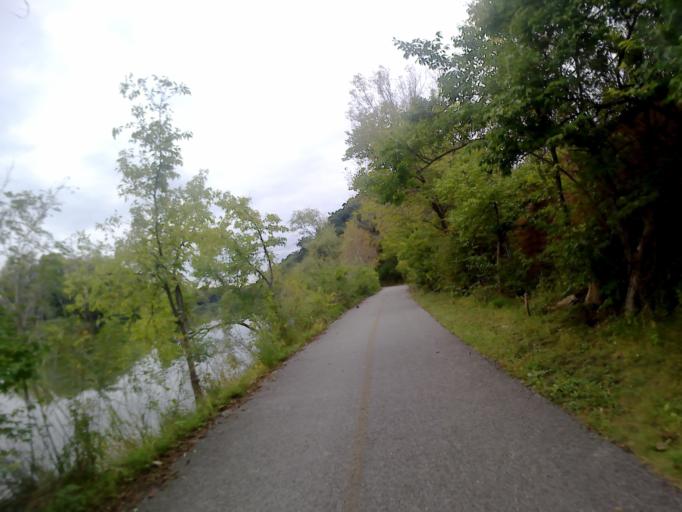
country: US
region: Illinois
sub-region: Kane County
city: North Aurora
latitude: 41.8112
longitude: -88.3233
